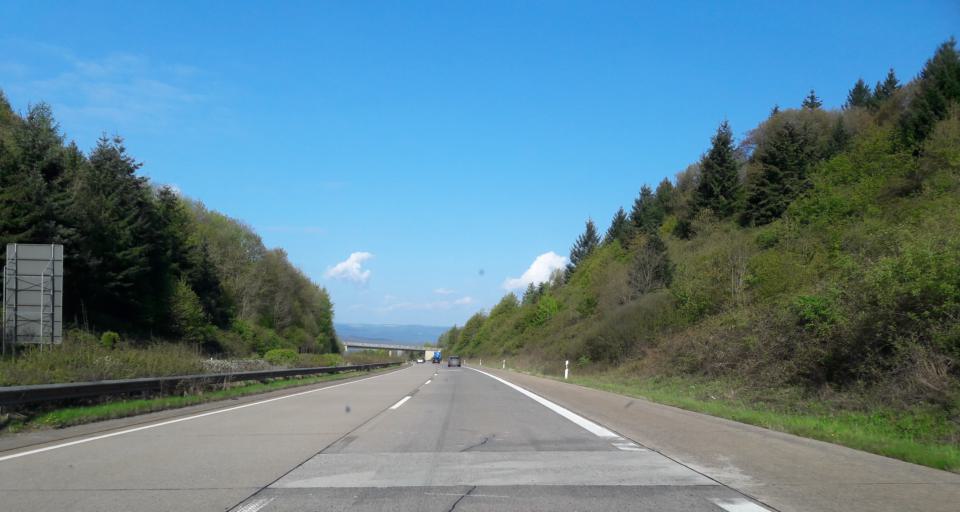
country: DE
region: Rheinland-Pfalz
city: Mehring
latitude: 49.7835
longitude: 6.8281
